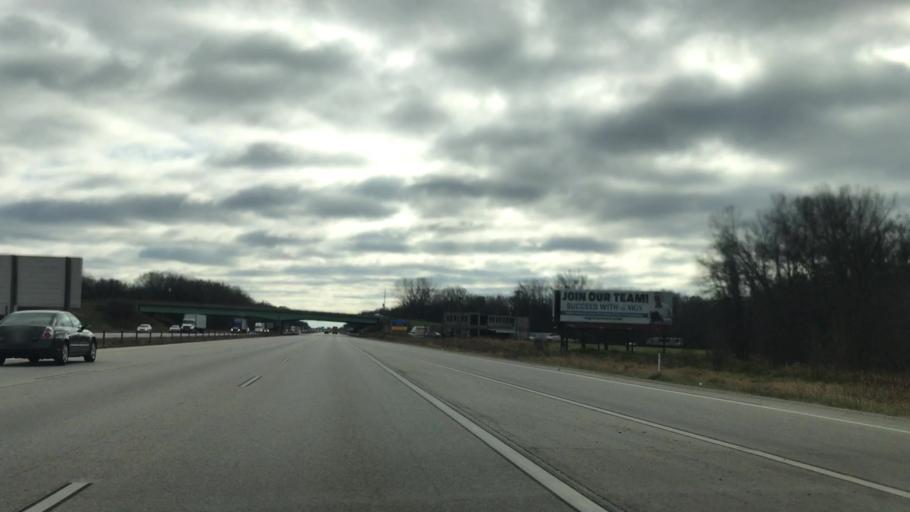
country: US
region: Wisconsin
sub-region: Washington County
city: Germantown
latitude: 43.2146
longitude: -88.1459
